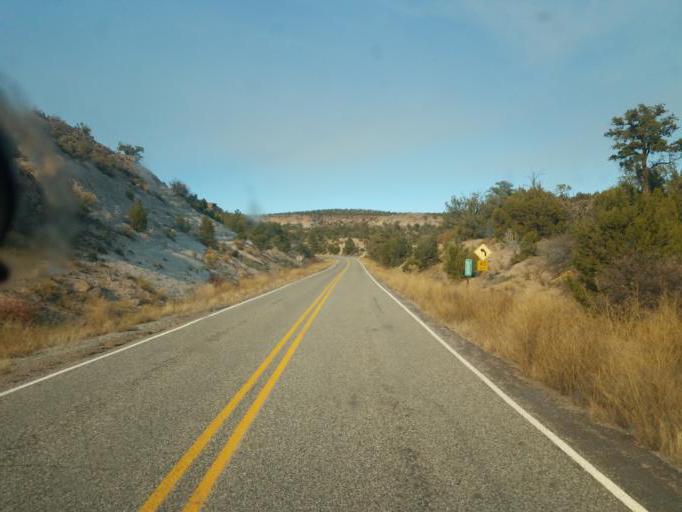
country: US
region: New Mexico
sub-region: Los Alamos County
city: White Rock
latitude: 35.8003
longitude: -106.2458
